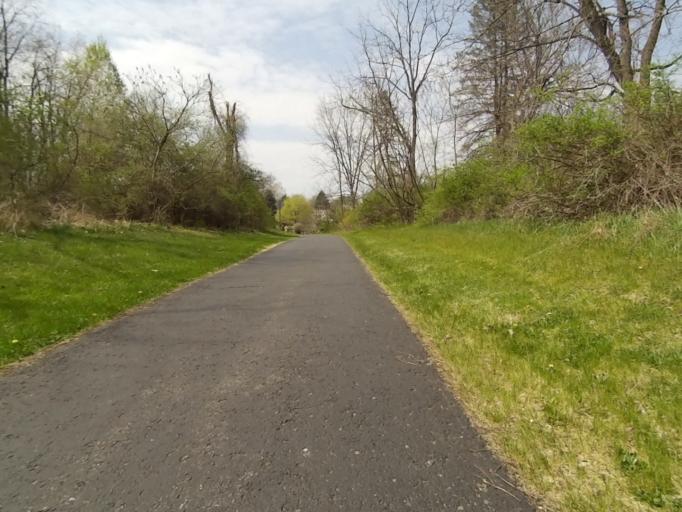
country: US
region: Pennsylvania
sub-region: Centre County
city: Park Forest Village
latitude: 40.7962
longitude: -77.8902
